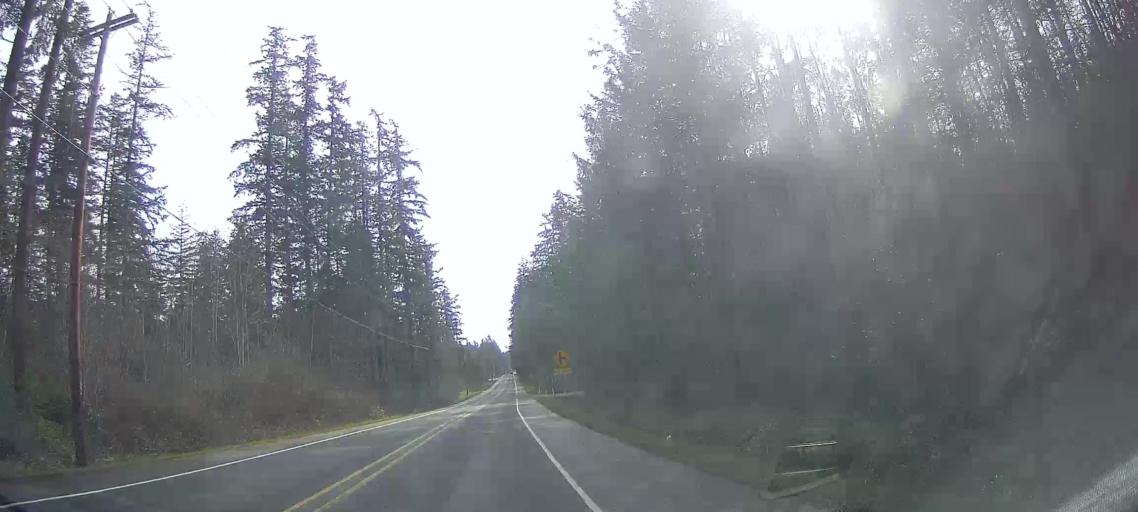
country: US
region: Washington
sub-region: Island County
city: Camano
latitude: 48.1484
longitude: -122.4718
